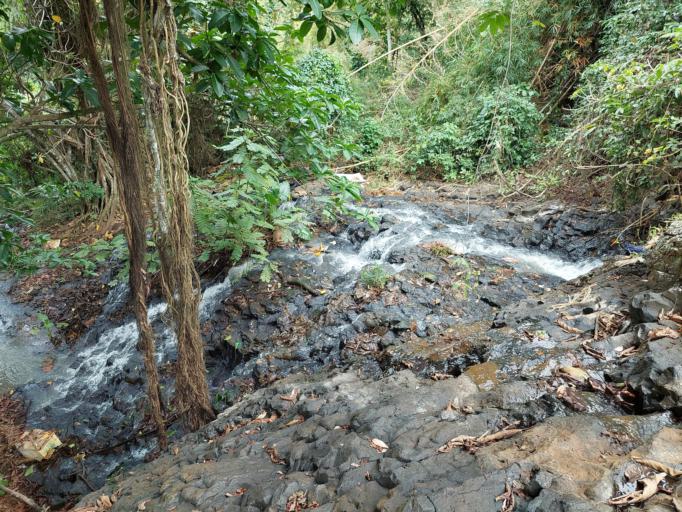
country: YT
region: Tsingoni
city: Tsingoni
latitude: -12.7878
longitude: 45.1055
